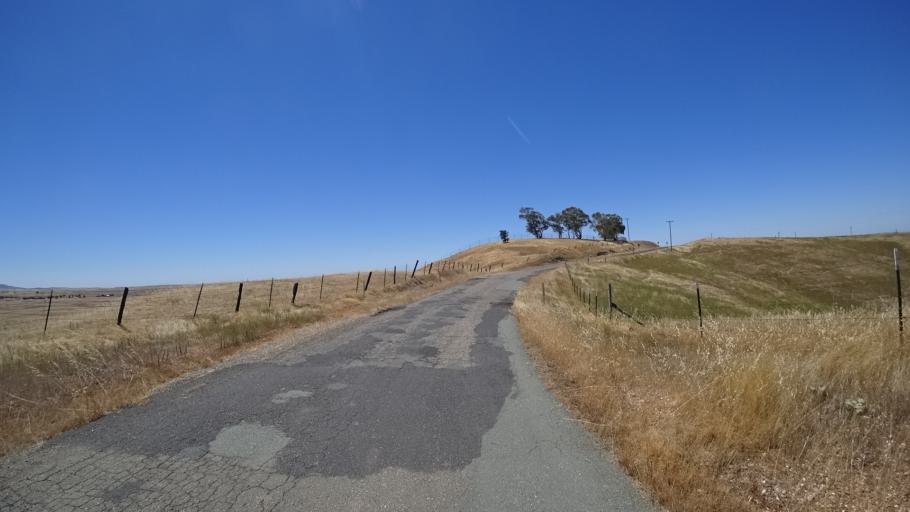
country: US
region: California
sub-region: Calaveras County
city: Rancho Calaveras
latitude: 38.0400
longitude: -120.8412
